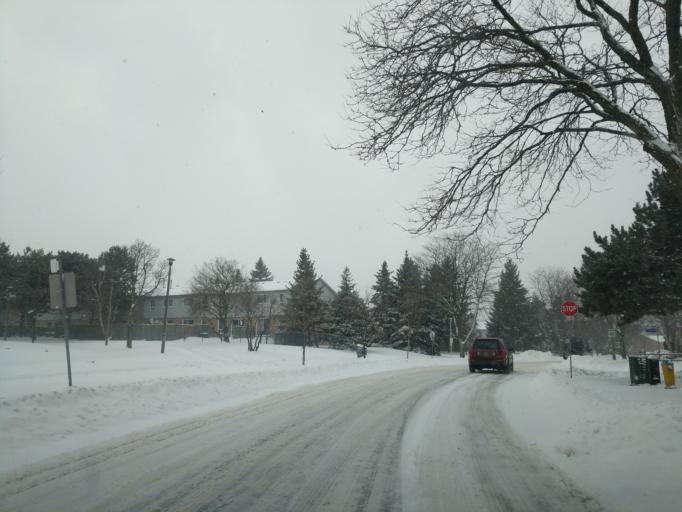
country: CA
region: Ontario
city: Scarborough
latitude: 43.8104
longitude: -79.2826
